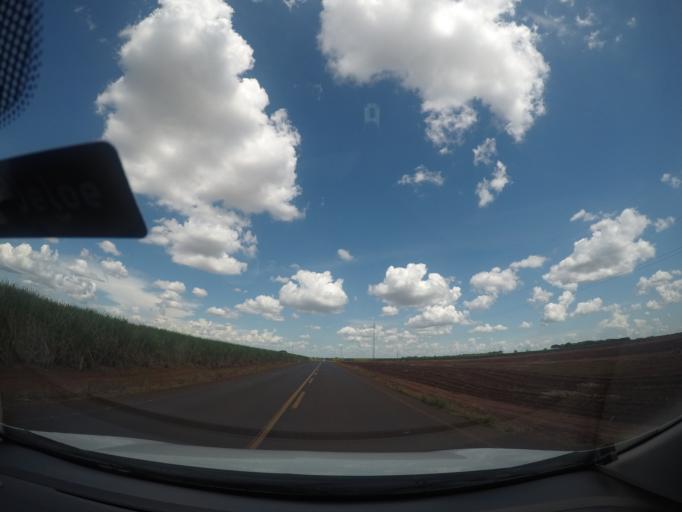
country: BR
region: Minas Gerais
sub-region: Frutal
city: Frutal
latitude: -19.8482
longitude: -48.7375
